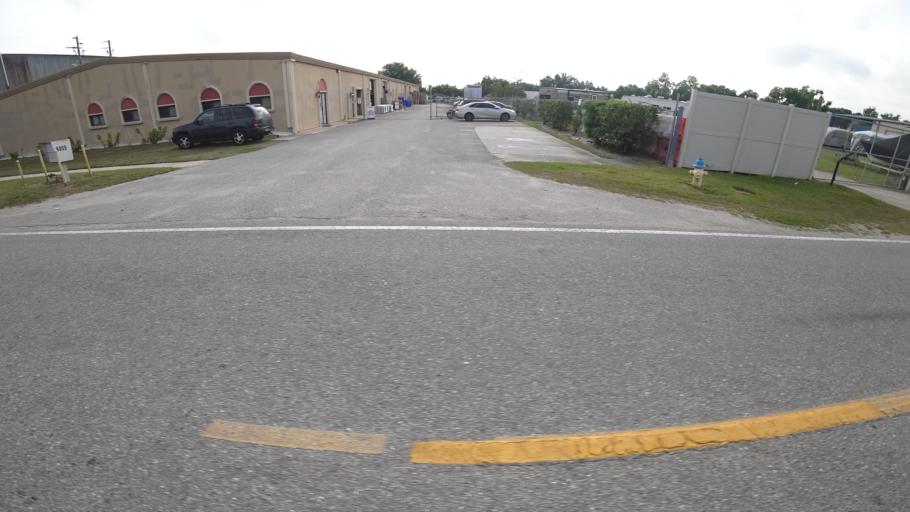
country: US
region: Florida
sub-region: Manatee County
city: Whitfield
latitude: 27.4196
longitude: -82.5219
